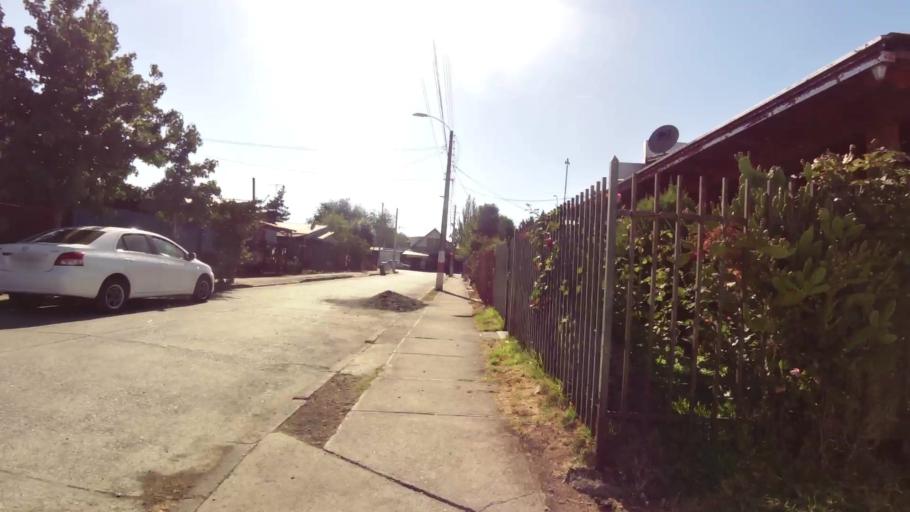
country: CL
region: Maule
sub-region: Provincia de Curico
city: Curico
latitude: -35.0016
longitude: -71.2467
